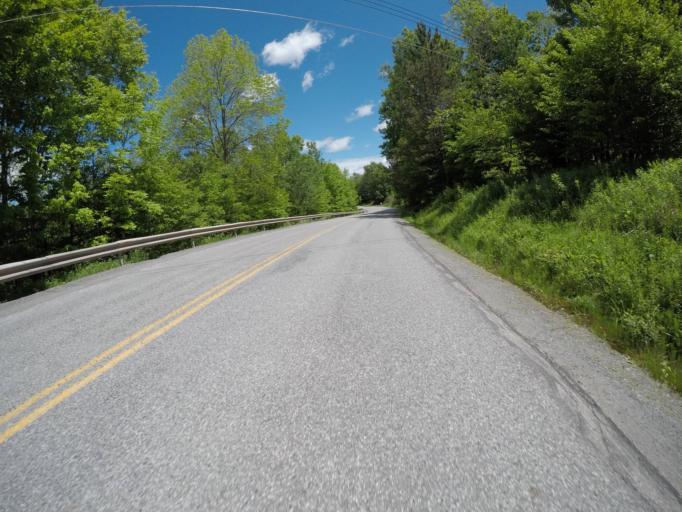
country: US
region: New York
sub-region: Delaware County
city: Stamford
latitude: 42.2302
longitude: -74.5621
